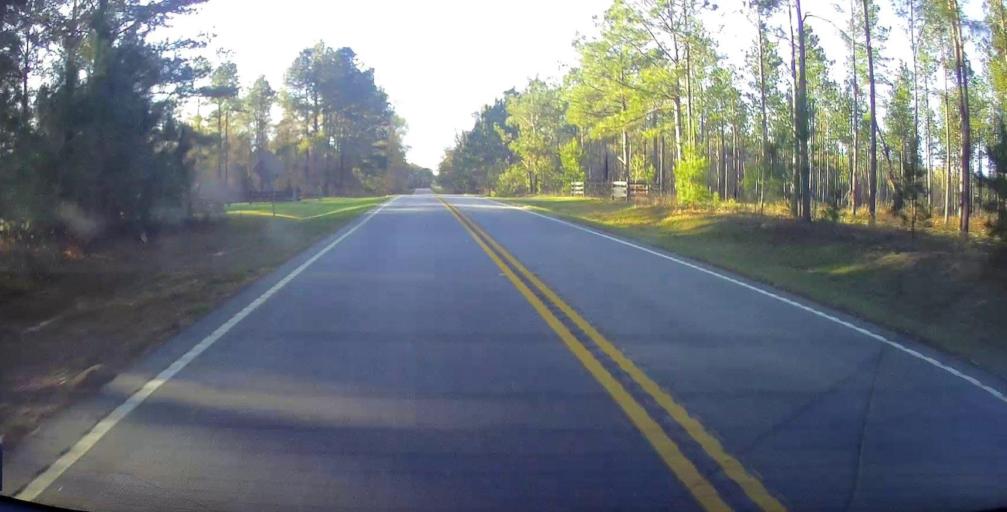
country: US
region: Georgia
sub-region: Wilcox County
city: Abbeville
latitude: 32.1397
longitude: -83.3412
